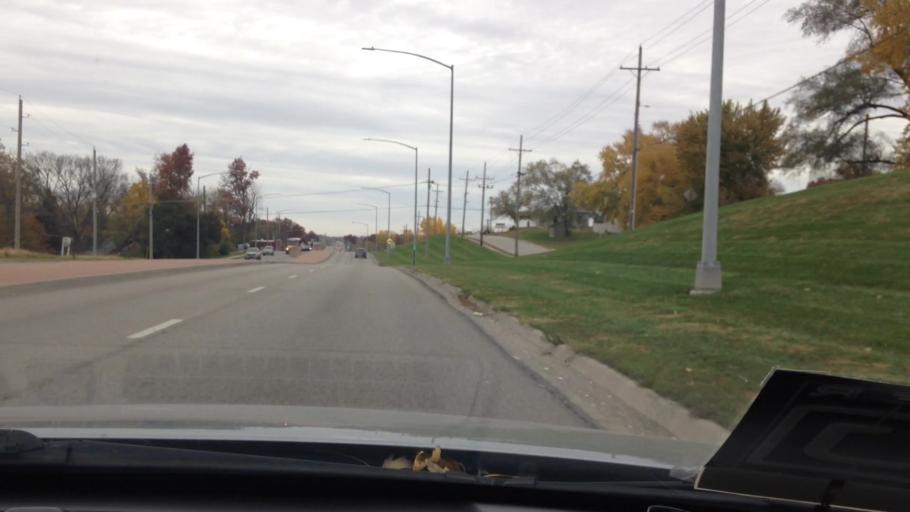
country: US
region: Kansas
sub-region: Leavenworth County
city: Lansing
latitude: 39.2459
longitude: -94.9001
